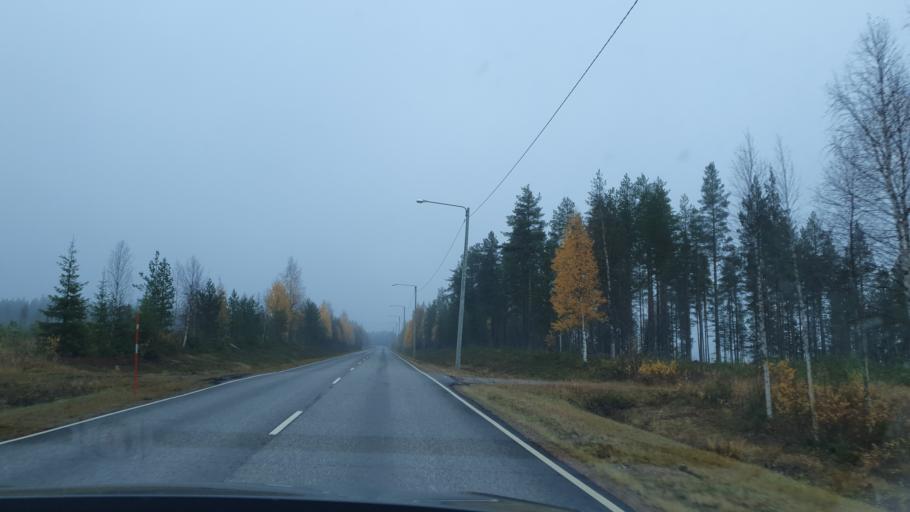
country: FI
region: Lapland
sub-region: Tunturi-Lappi
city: Kittilae
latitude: 67.0374
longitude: 25.1027
